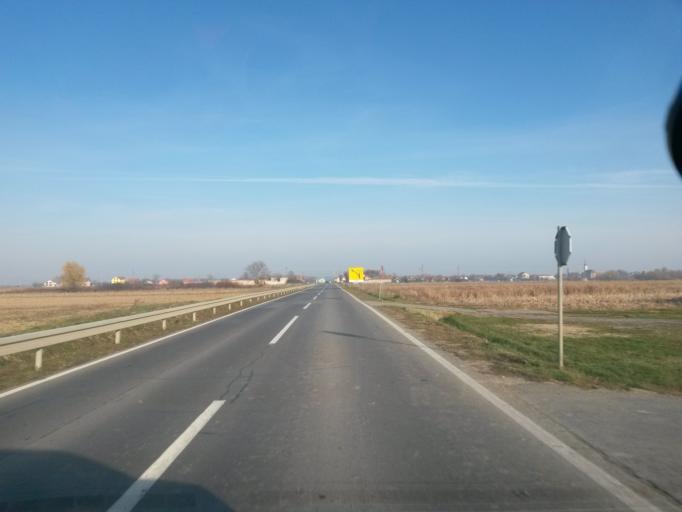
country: HR
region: Osjecko-Baranjska
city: Laslovo
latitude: 45.4142
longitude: 18.6837
